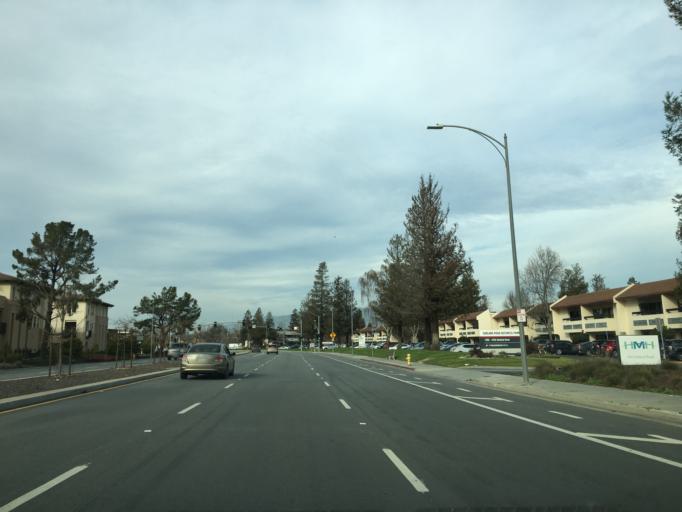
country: US
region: California
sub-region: Santa Clara County
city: San Jose
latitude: 37.3795
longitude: -121.8954
